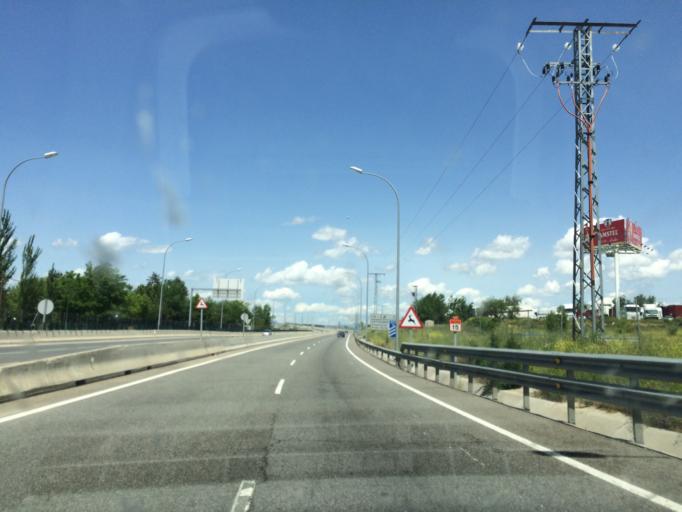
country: ES
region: Madrid
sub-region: Provincia de Madrid
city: Cobena
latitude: 40.5856
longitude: -3.5597
